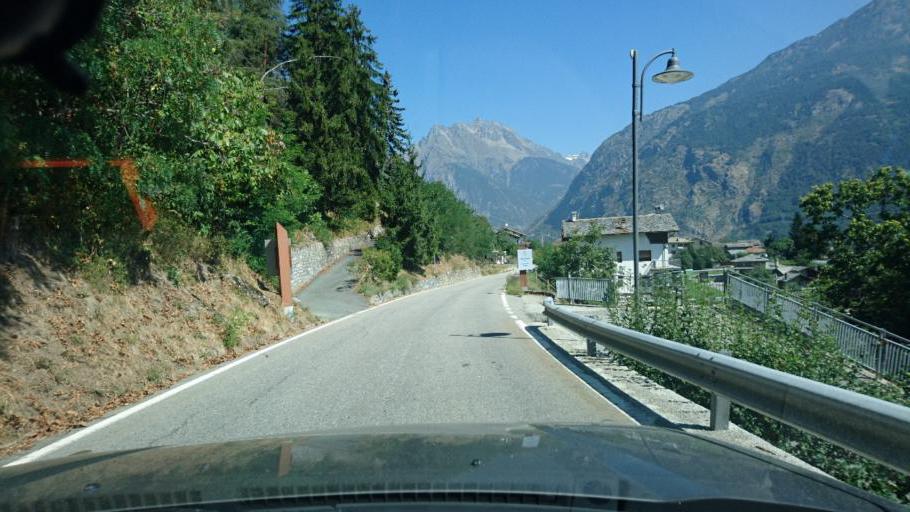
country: IT
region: Aosta Valley
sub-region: Valle d'Aosta
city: Gignod
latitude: 45.7814
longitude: 7.2935
